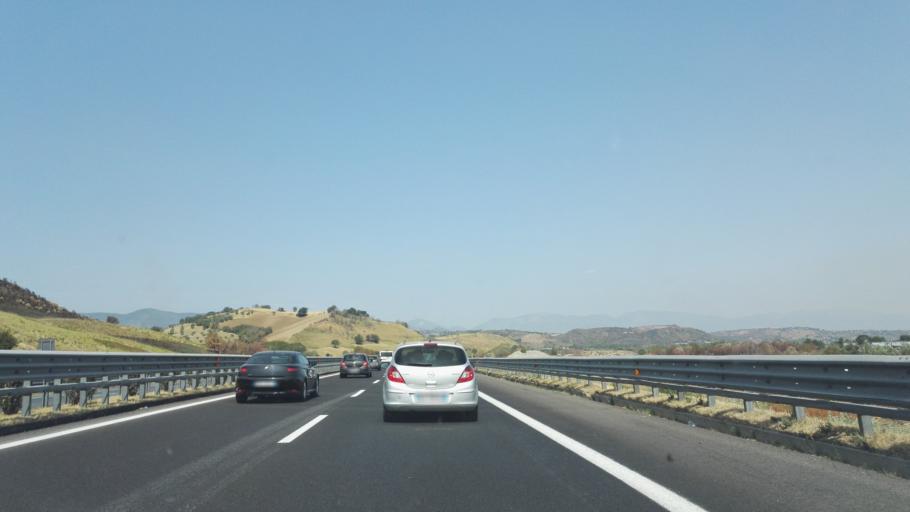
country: IT
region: Calabria
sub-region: Provincia di Cosenza
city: Taverna
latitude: 39.4568
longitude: 16.2306
